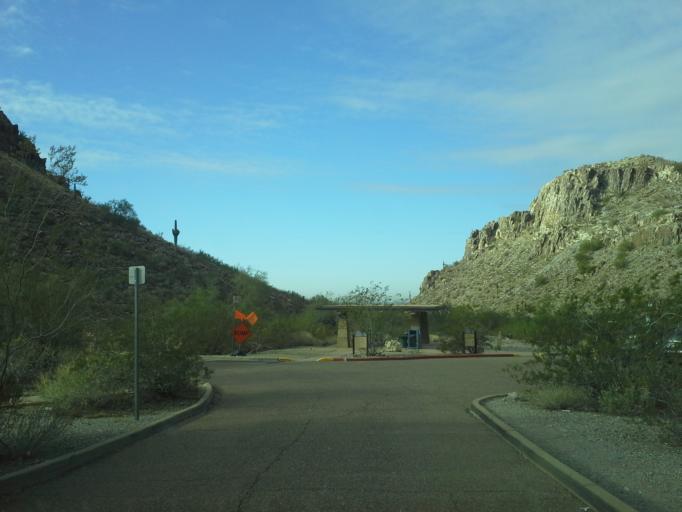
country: US
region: Arizona
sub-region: Maricopa County
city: Paradise Valley
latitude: 33.5399
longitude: -112.0214
